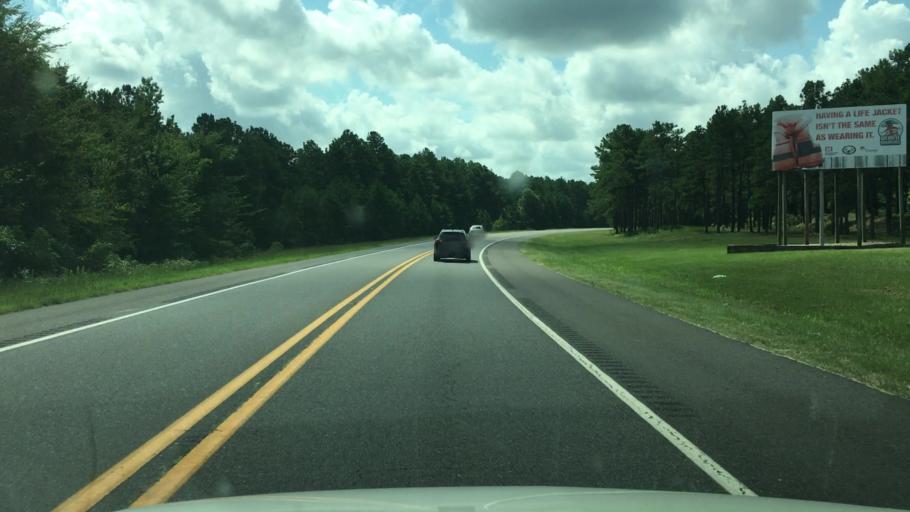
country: US
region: Arkansas
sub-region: Clark County
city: Arkadelphia
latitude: 34.2272
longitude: -93.0895
